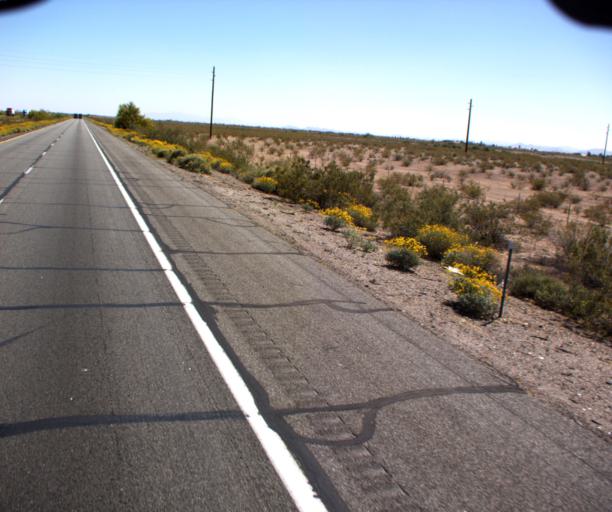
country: US
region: Arizona
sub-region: Maricopa County
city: Buckeye
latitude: 33.4744
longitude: -112.8346
